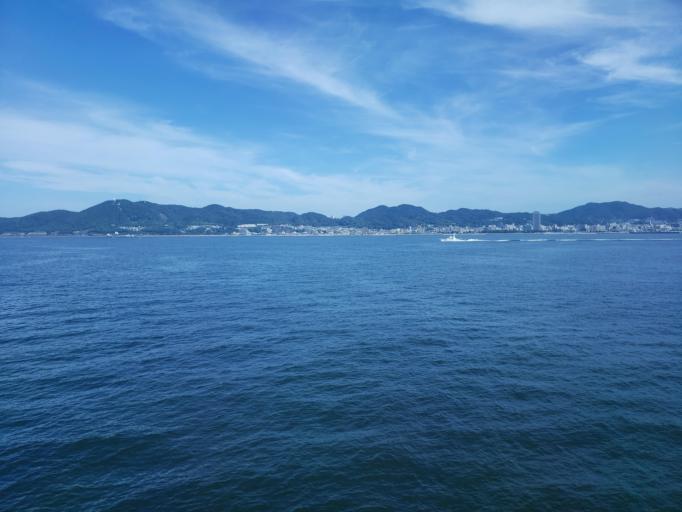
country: JP
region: Hyogo
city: Kobe
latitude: 34.6171
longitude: 135.1286
